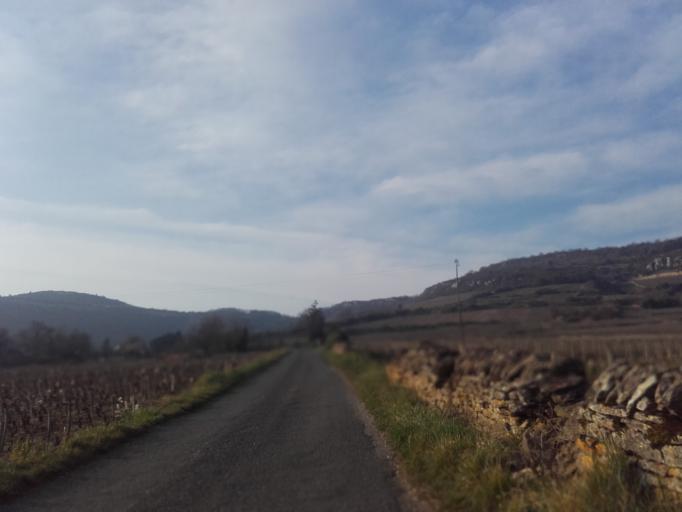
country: FR
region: Bourgogne
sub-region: Departement de Saone-et-Loire
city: Chagny
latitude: 46.9131
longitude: 4.6890
